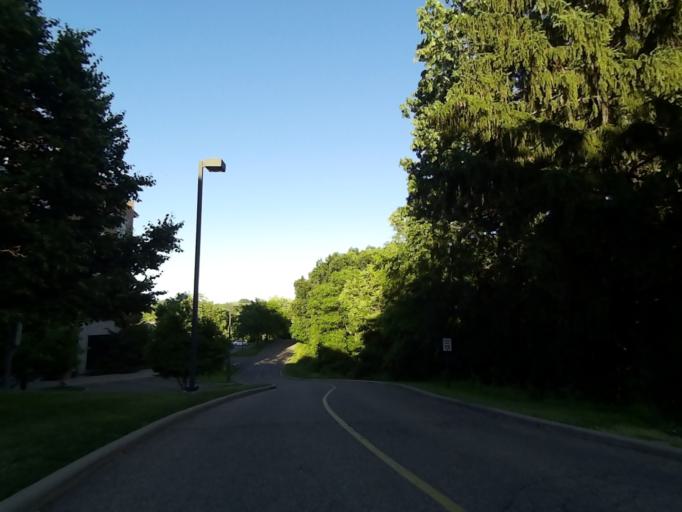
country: US
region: Ohio
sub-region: Jefferson County
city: Steubenville
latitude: 40.3758
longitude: -80.6224
